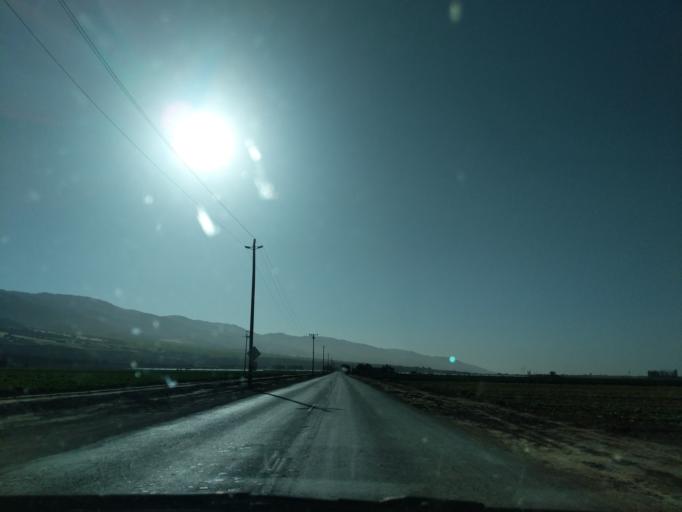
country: US
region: California
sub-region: Monterey County
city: Soledad
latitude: 36.4040
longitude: -121.3620
